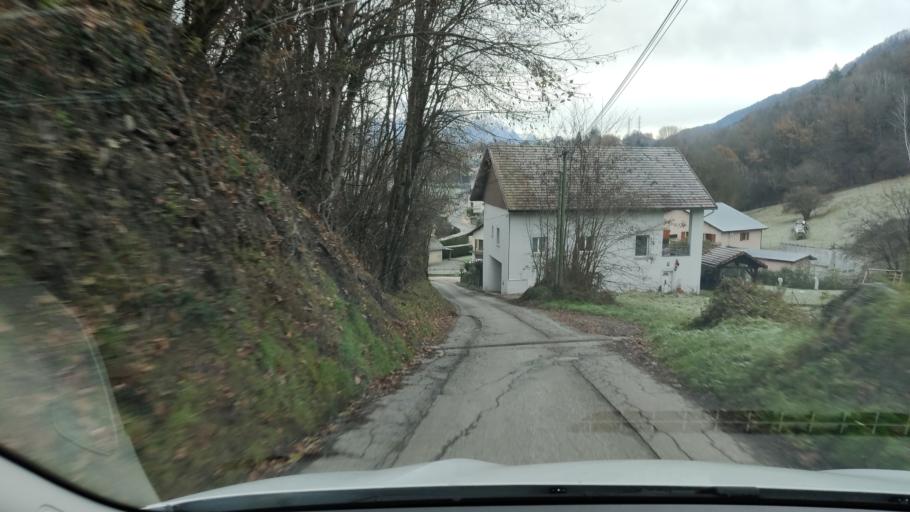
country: FR
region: Rhone-Alpes
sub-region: Departement de la Savoie
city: Montmelian
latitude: 45.4610
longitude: 6.0588
